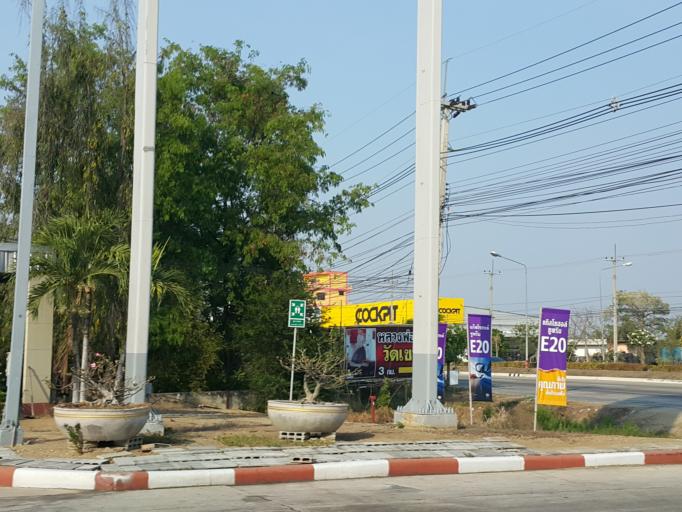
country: TH
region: Suphan Buri
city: Doembang Nangbuat
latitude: 14.8040
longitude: 100.1133
